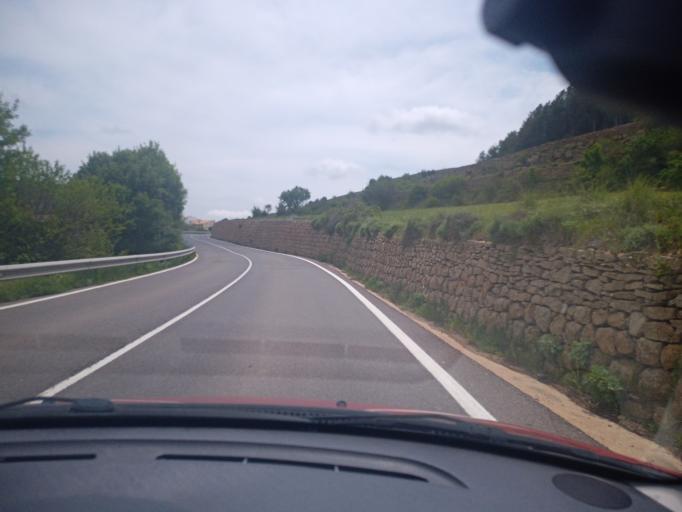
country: ES
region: Valencia
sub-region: Provincia de Castello
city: Ares del Maestre
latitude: 40.4571
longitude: -0.1466
